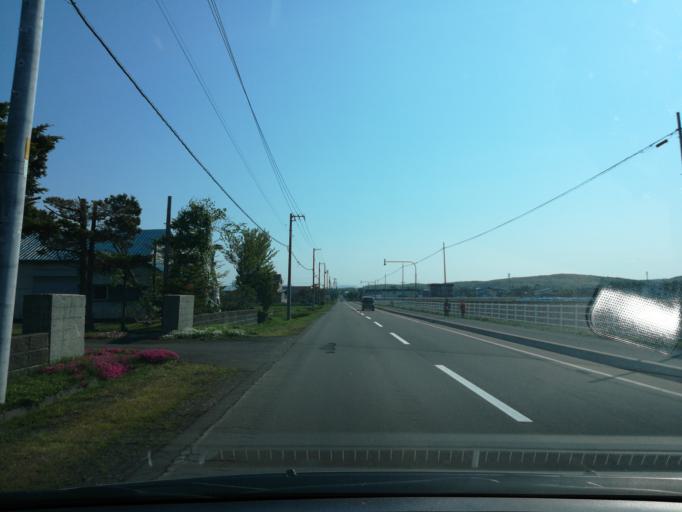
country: JP
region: Hokkaido
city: Iwamizawa
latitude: 43.1698
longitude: 141.7528
